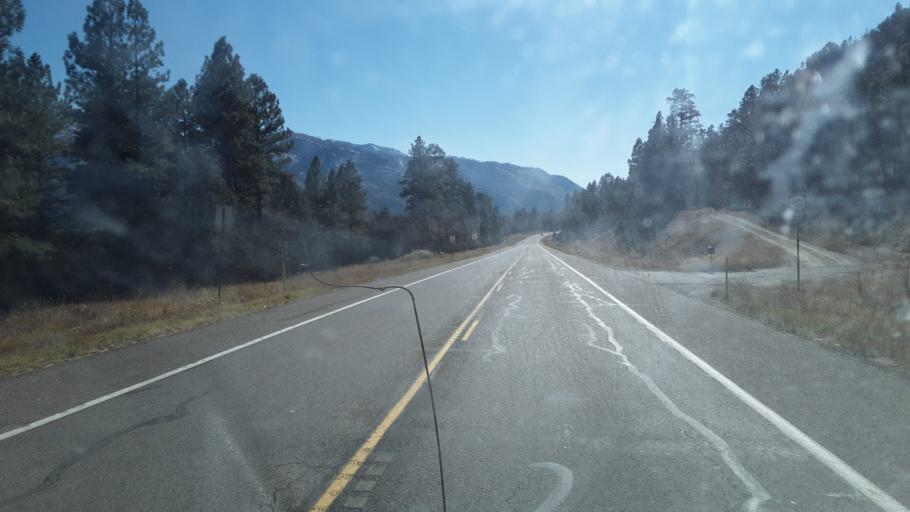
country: US
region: Colorado
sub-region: La Plata County
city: Durango
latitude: 37.4481
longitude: -107.8070
